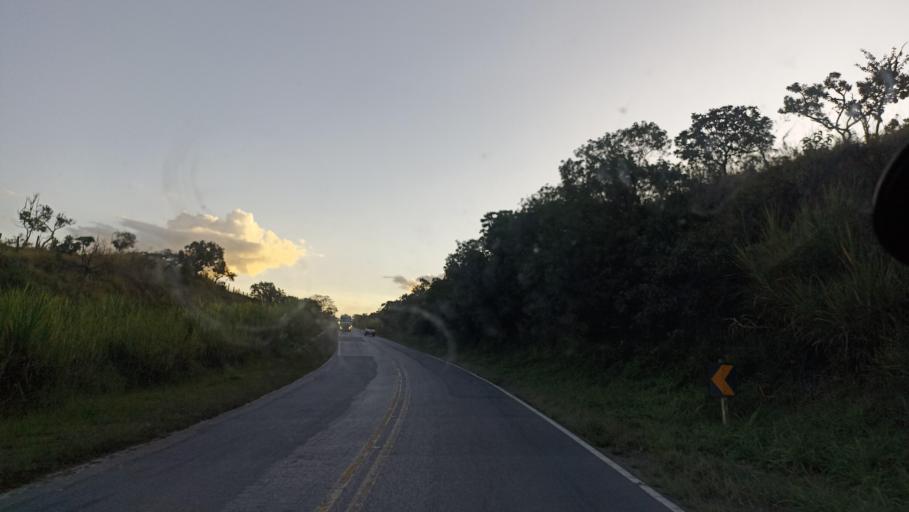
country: BR
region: Minas Gerais
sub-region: Sao Joao Del Rei
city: Sao Joao del Rei
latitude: -21.2297
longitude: -44.3830
